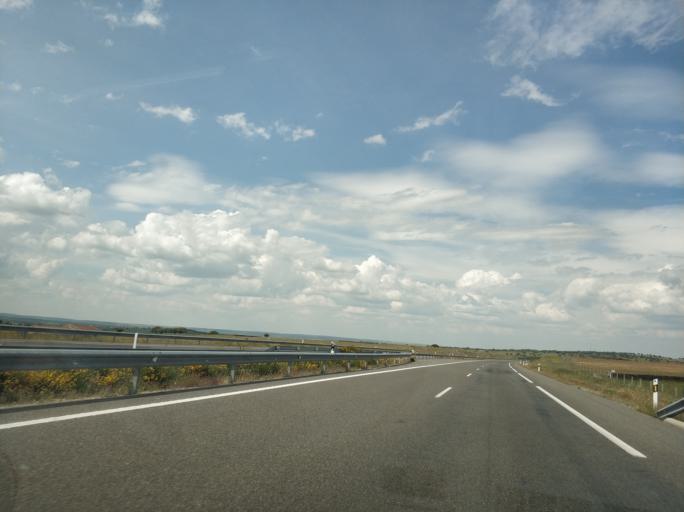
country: ES
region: Castille and Leon
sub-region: Provincia de Salamanca
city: Pizarral
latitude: 40.5973
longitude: -5.6518
